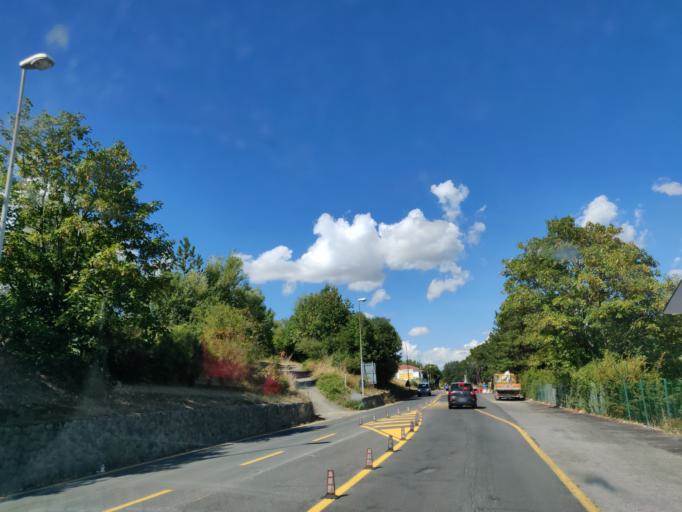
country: IT
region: Tuscany
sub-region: Provincia di Siena
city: Abbadia San Salvatore
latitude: 42.8922
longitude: 11.6674
